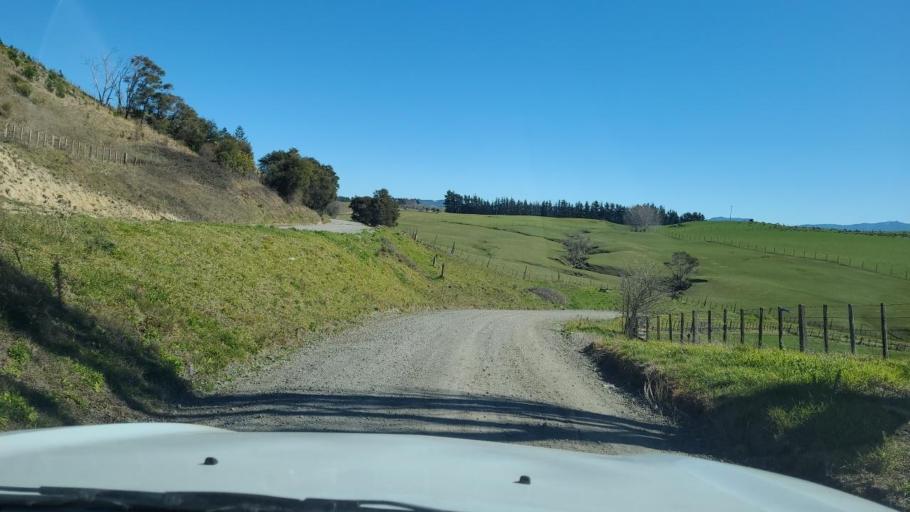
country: NZ
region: Hawke's Bay
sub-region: Napier City
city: Taradale
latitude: -39.4461
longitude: 176.5575
